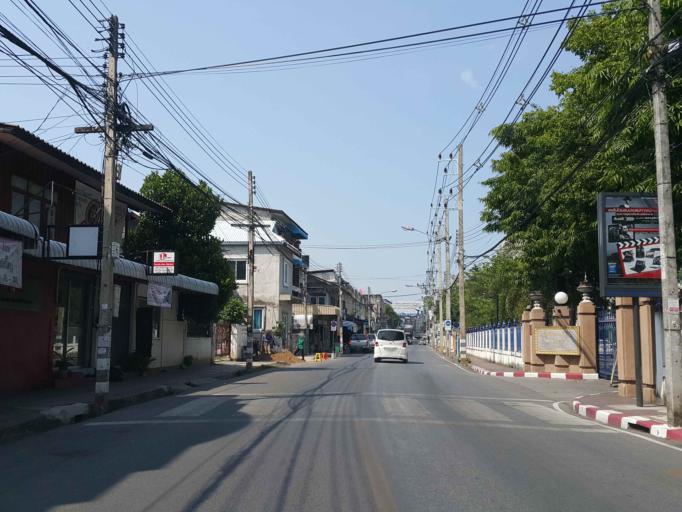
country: TH
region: Chiang Mai
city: Chiang Mai
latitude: 18.7731
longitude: 99.0002
